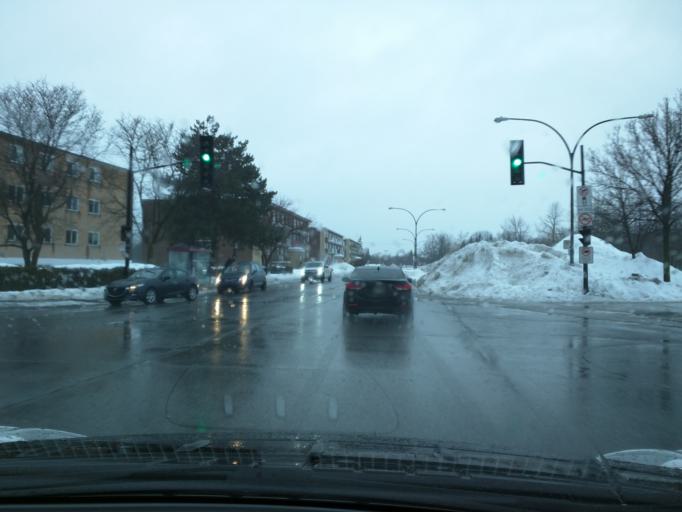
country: CA
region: Quebec
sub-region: Monteregie
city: Longueuil
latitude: 45.5418
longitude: -73.4715
